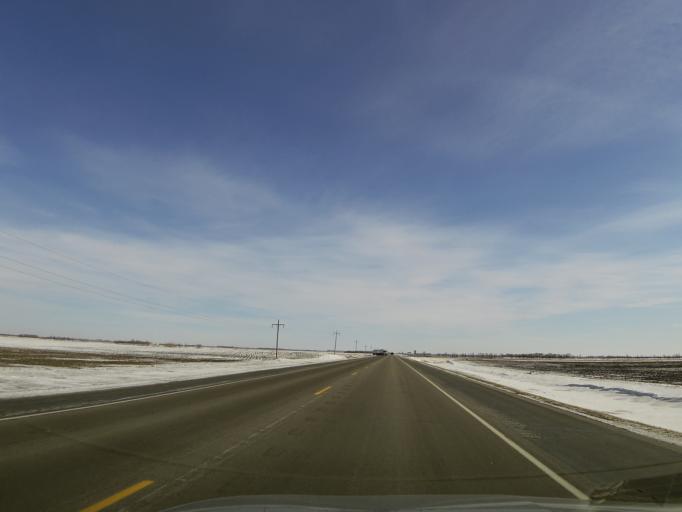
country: US
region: North Dakota
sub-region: Walsh County
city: Grafton
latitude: 48.4123
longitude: -97.3039
